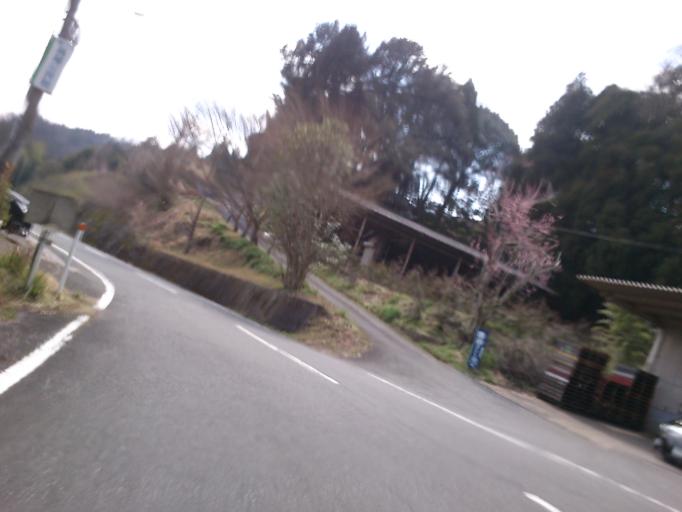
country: JP
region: Mie
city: Ueno-ebisumachi
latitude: 34.7274
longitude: 136.0004
